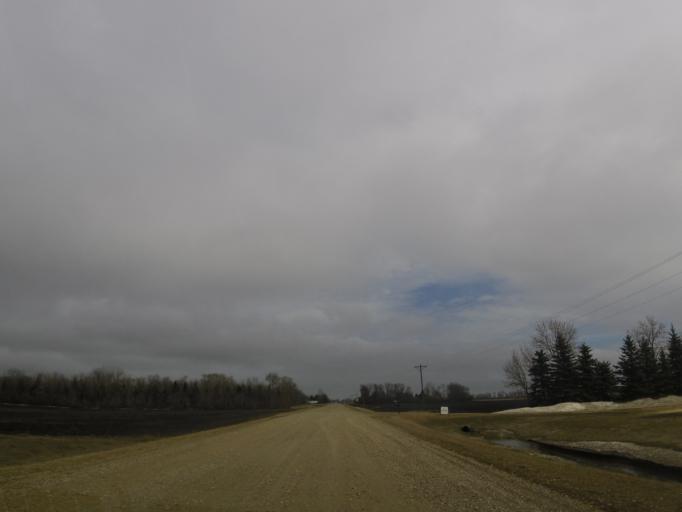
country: US
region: North Dakota
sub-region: Walsh County
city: Grafton
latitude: 48.4262
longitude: -97.3291
